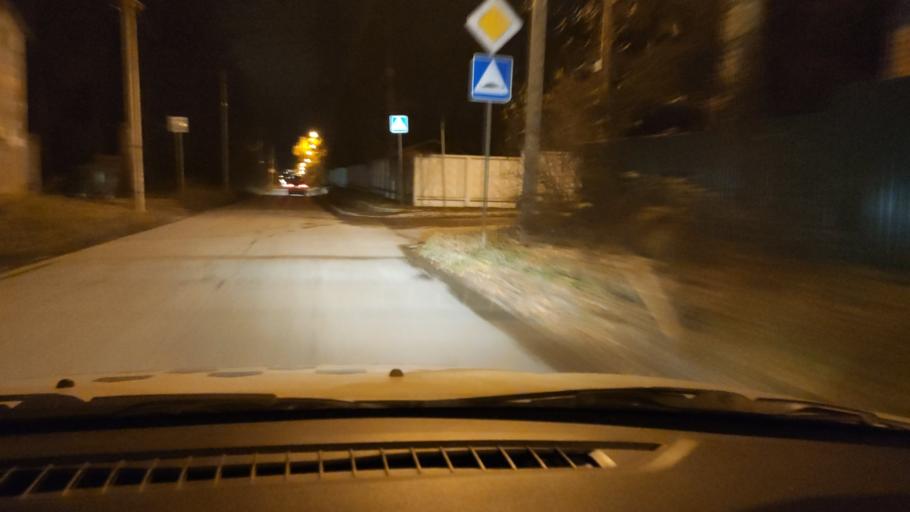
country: RU
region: Perm
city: Kondratovo
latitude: 58.0527
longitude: 56.1219
